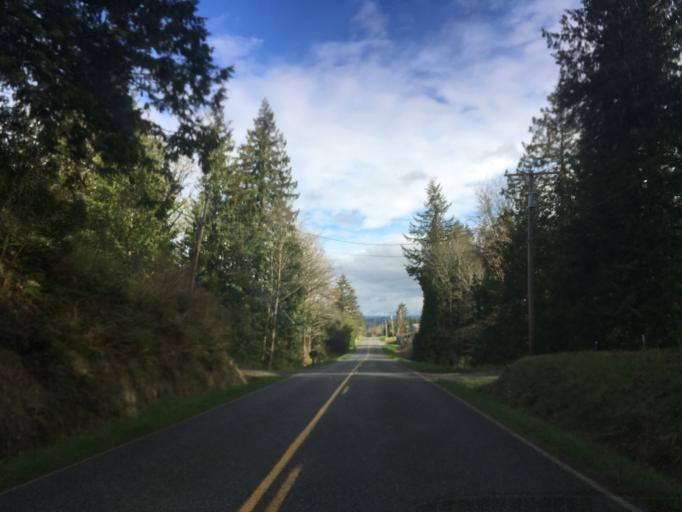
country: US
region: Washington
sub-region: Whatcom County
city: Sudden Valley
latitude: 48.7995
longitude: -122.3439
